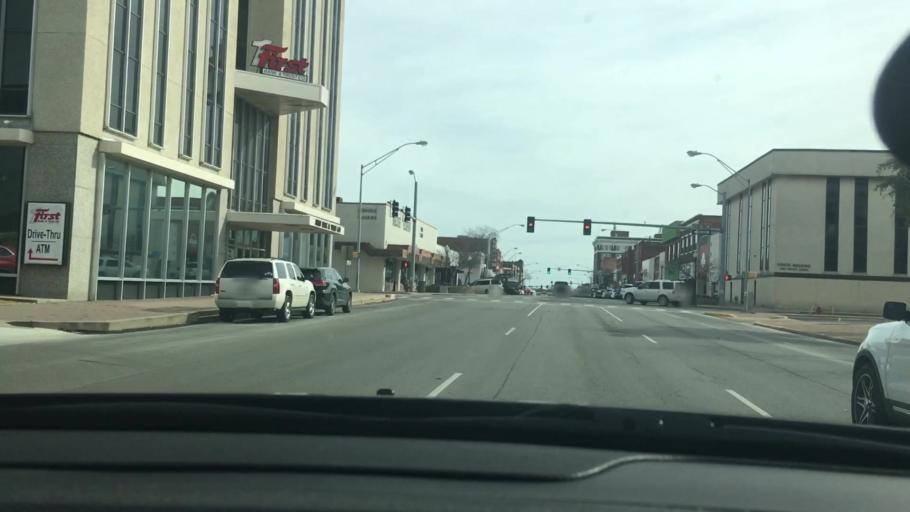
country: US
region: Oklahoma
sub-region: Carter County
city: Ardmore
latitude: 34.1736
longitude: -97.1326
